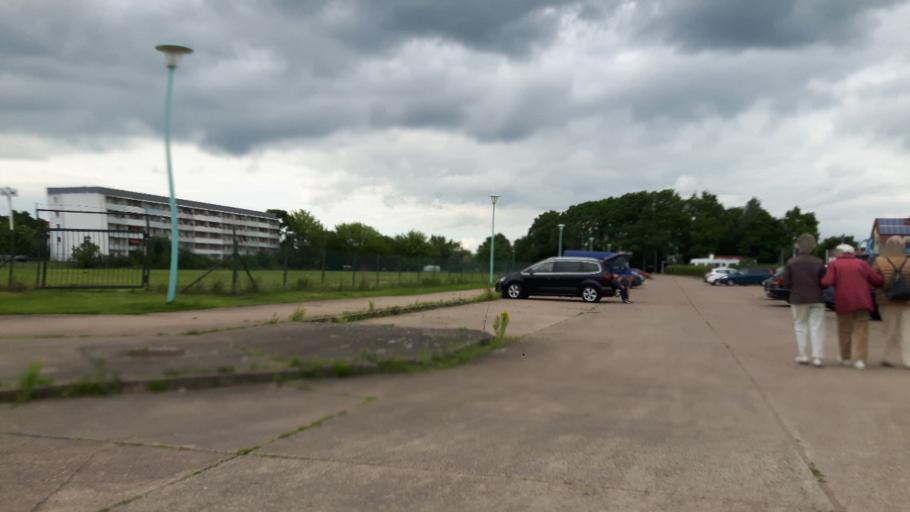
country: DE
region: Brandenburg
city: Schwedt (Oder)
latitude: 53.0571
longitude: 14.2973
